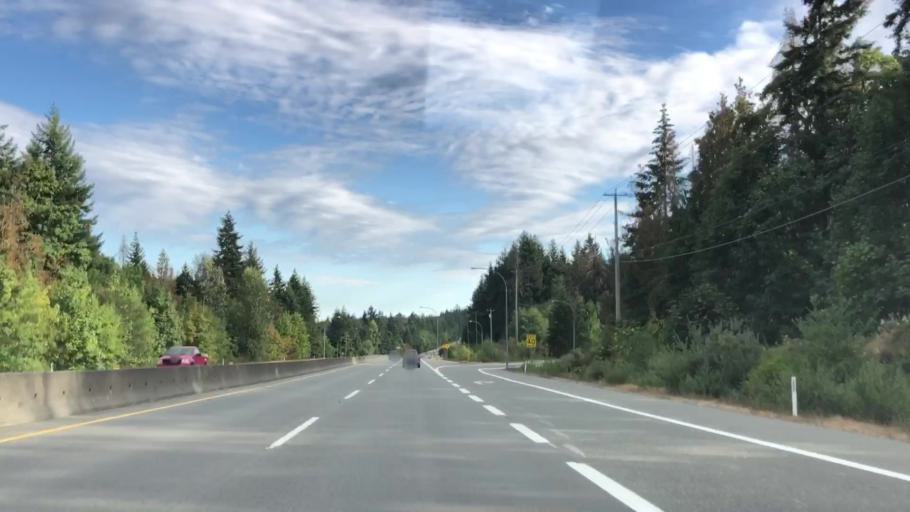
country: CA
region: British Columbia
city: North Saanich
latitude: 48.6156
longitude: -123.5419
